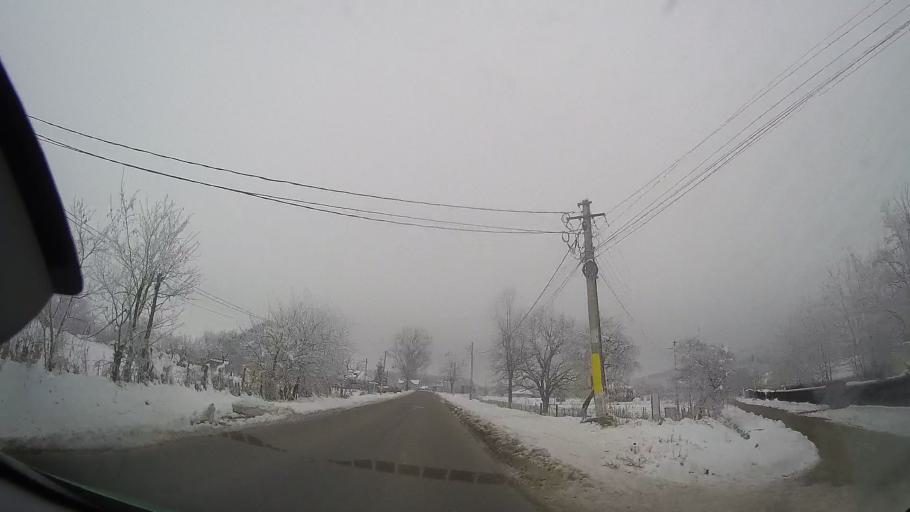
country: RO
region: Neamt
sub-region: Comuna Horia
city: Cotu Vames
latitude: 46.8736
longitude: 26.9778
